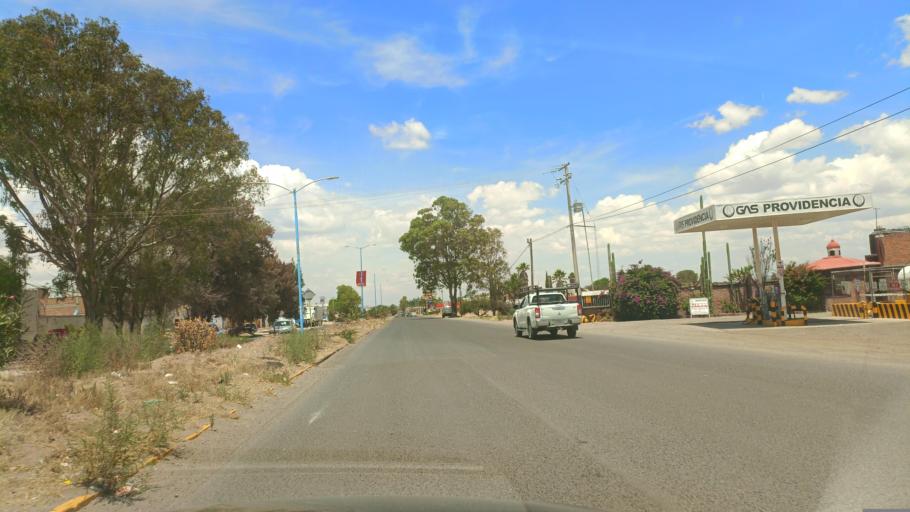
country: MX
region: Guanajuato
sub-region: San Luis de la Paz
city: San Ignacio
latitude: 21.2931
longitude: -100.5382
